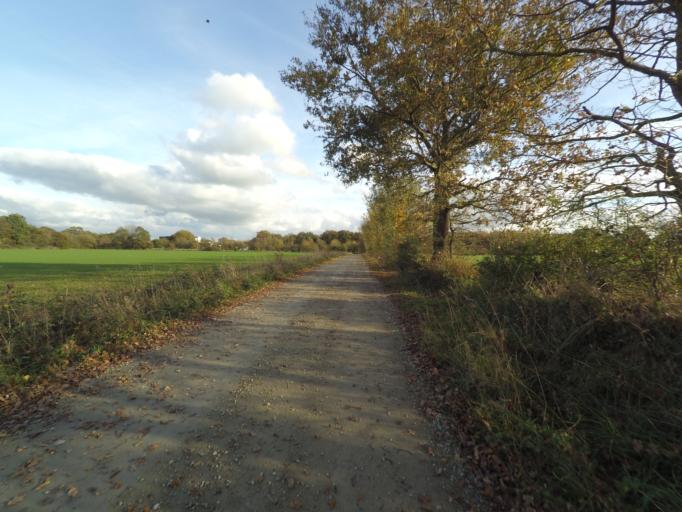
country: FR
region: Pays de la Loire
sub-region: Departement de la Vendee
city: Saint-Hilaire-de-Loulay
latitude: 47.0080
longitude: -1.3424
